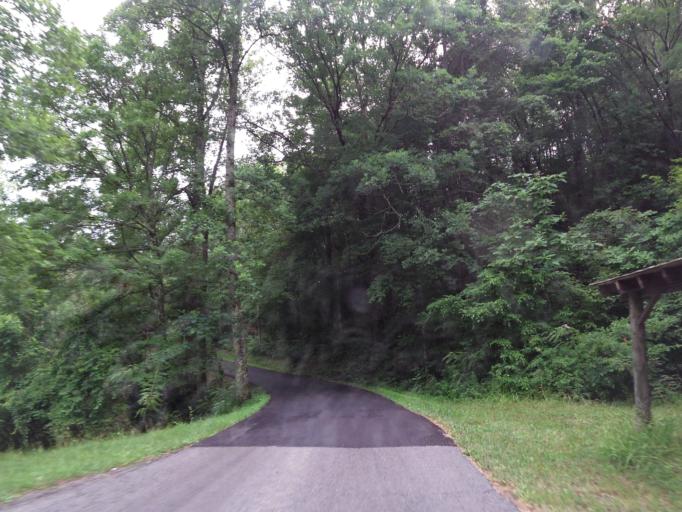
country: US
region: Tennessee
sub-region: Blount County
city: Wildwood
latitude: 35.7436
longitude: -83.7947
